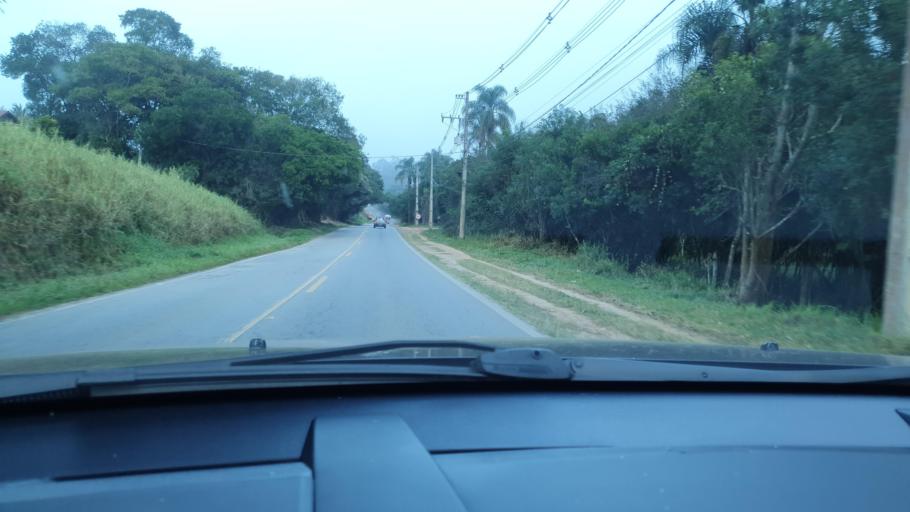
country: BR
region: Sao Paulo
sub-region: Ibiuna
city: Ibiuna
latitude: -23.6798
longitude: -47.2459
